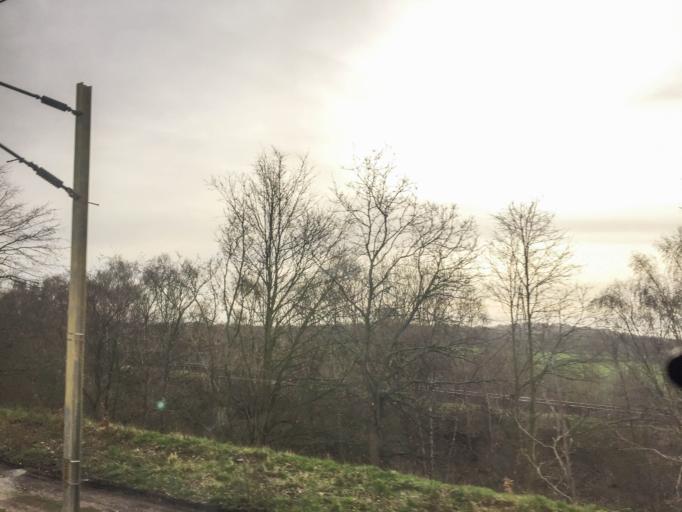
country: GB
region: England
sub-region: Borough of Halton
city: Daresbury
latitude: 53.3684
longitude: -2.6150
